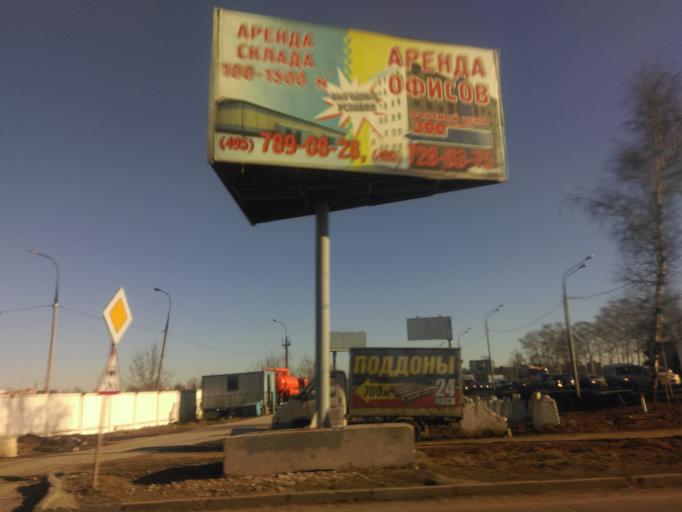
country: RU
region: Moskovskaya
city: Odintsovo
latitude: 55.6693
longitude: 37.3103
